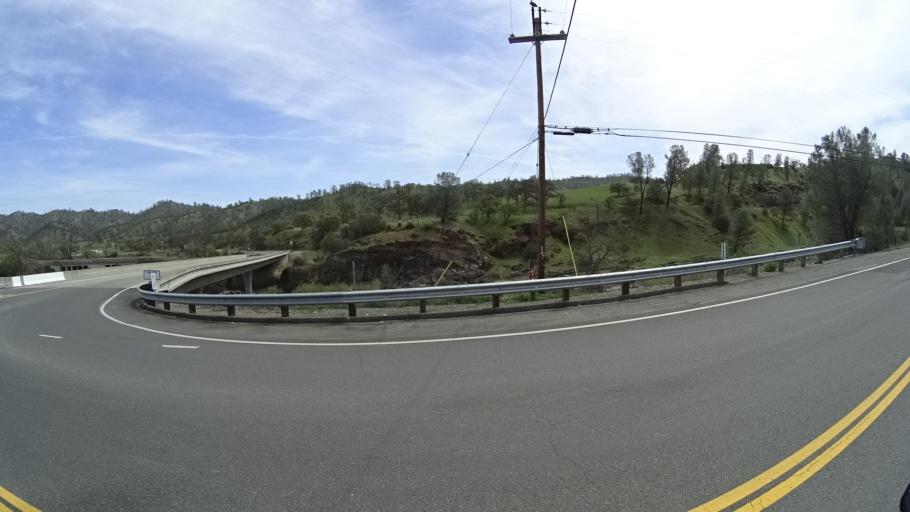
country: US
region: California
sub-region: Glenn County
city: Willows
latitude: 39.6116
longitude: -122.5306
